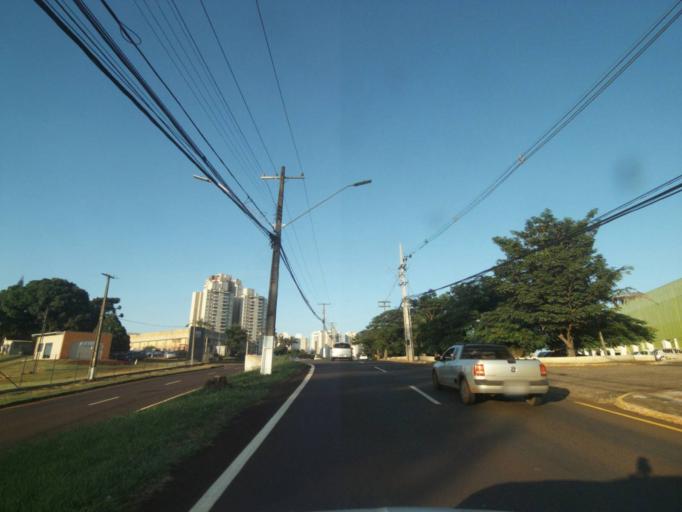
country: BR
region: Parana
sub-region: Londrina
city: Londrina
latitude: -23.3406
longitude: -51.1877
